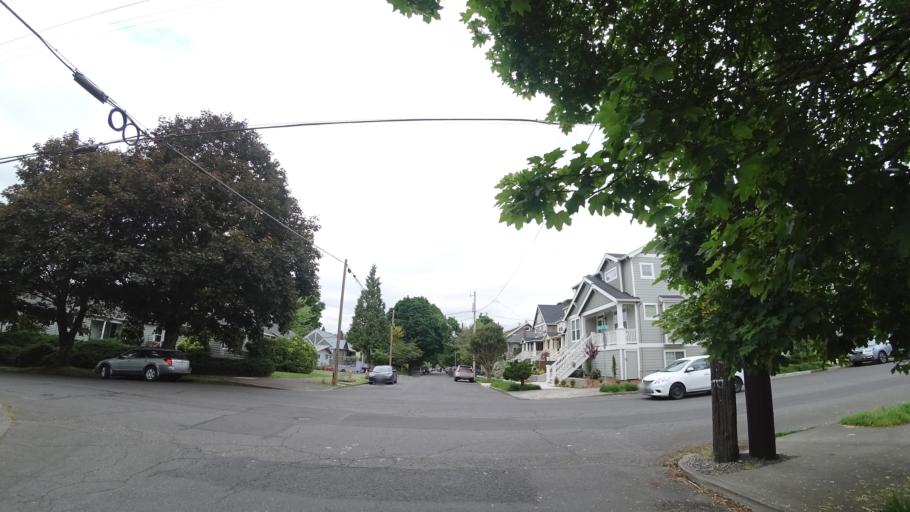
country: US
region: Oregon
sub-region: Multnomah County
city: Portland
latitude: 45.4991
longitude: -122.6334
